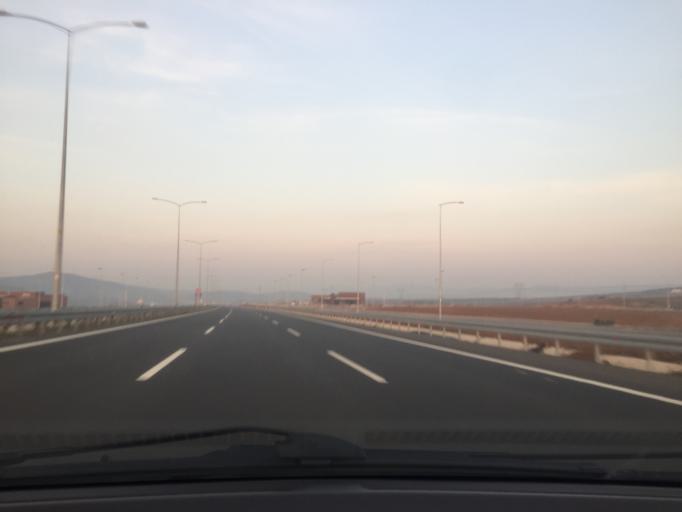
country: TR
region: Bursa
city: Mahmudiye
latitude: 40.2726
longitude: 28.6047
